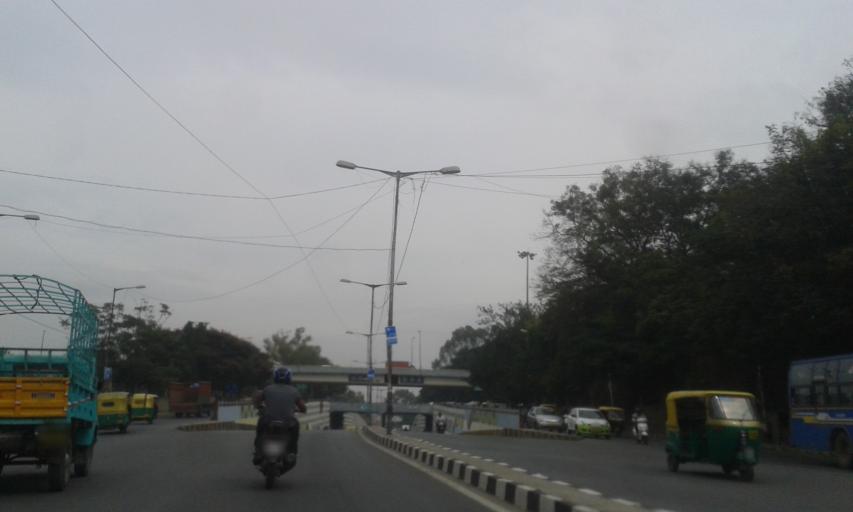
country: IN
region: Karnataka
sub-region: Bangalore Urban
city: Bangalore
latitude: 12.9355
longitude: 77.6013
